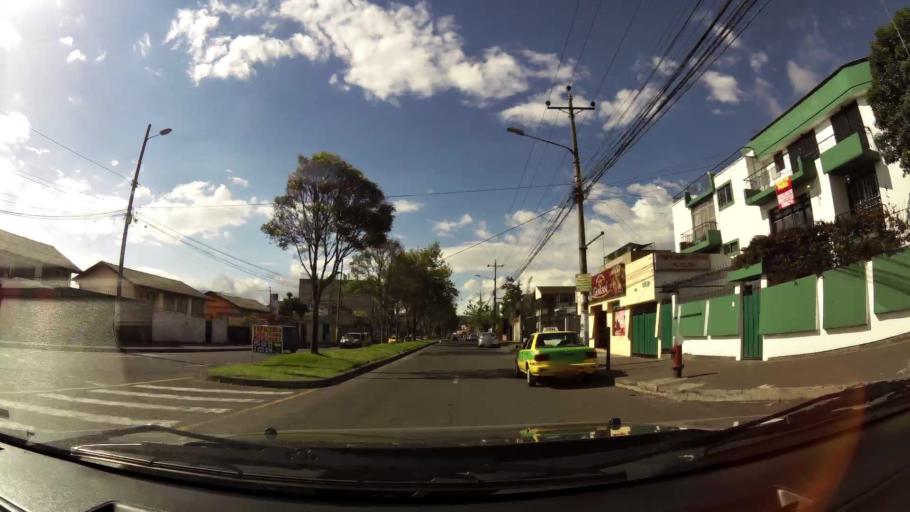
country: EC
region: Pichincha
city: Quito
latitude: -0.1213
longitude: -78.4847
